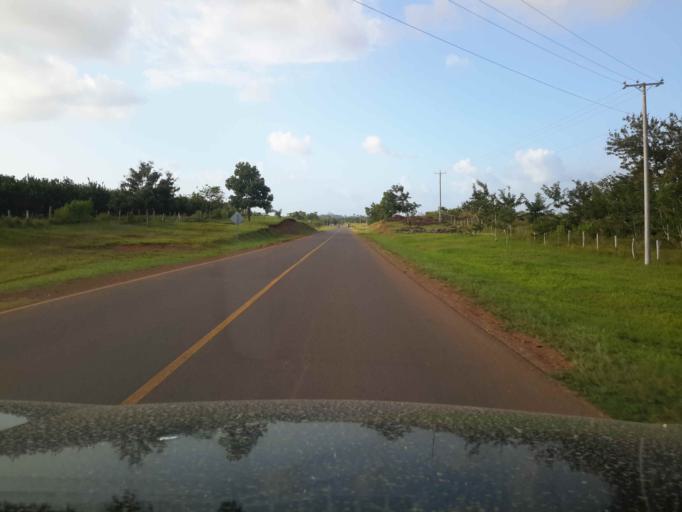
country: NI
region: Rio San Juan
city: San Carlos
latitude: 11.1550
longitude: -84.6562
